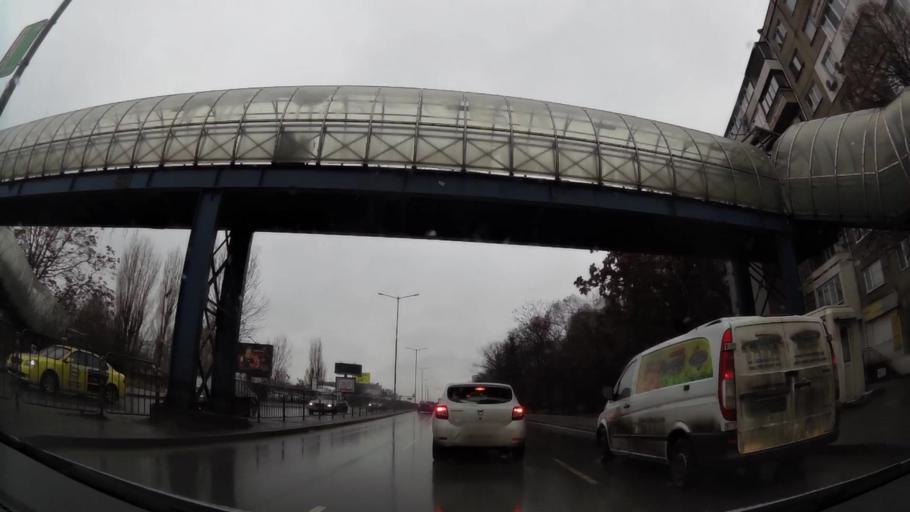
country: BG
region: Sofia-Capital
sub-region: Stolichna Obshtina
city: Sofia
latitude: 42.6548
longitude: 23.3813
